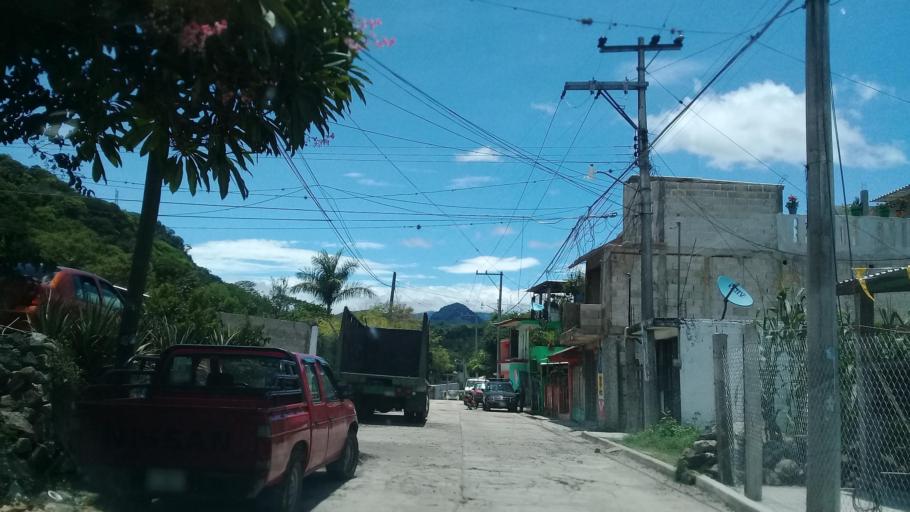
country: MX
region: Veracruz
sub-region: Naolinco
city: El Espinal
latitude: 19.5875
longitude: -96.8752
